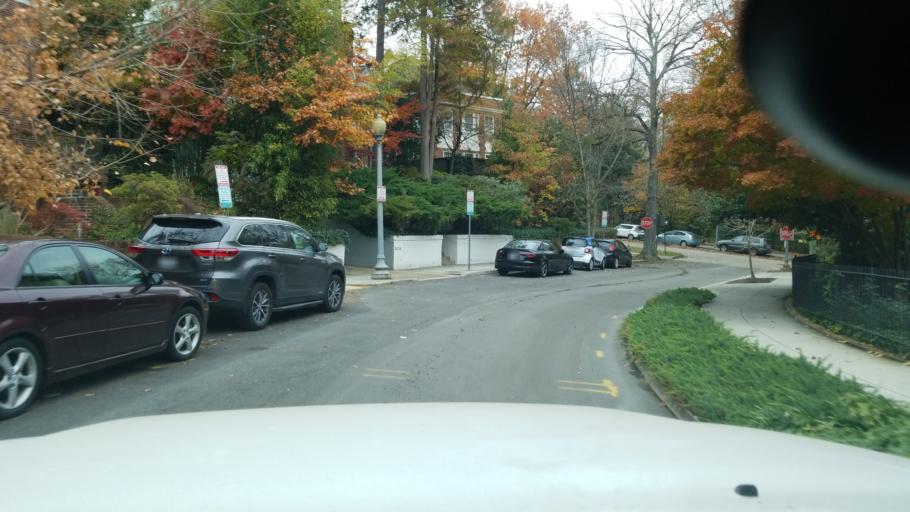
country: US
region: Washington, D.C.
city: Washington, D.C.
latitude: 38.9297
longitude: -77.0606
